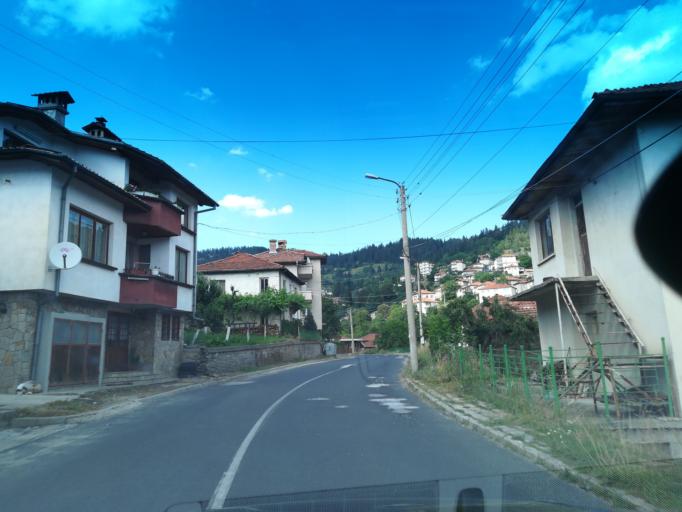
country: BG
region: Smolyan
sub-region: Obshtina Smolyan
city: Smolyan
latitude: 41.6557
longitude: 24.7738
